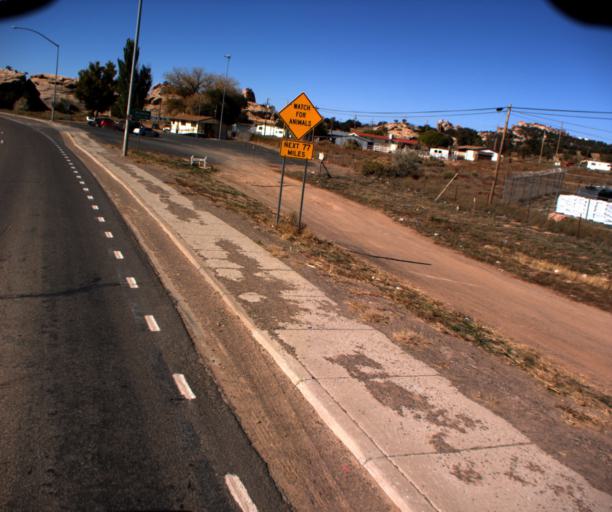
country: US
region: Arizona
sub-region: Apache County
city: Window Rock
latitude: 35.6622
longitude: -109.0461
